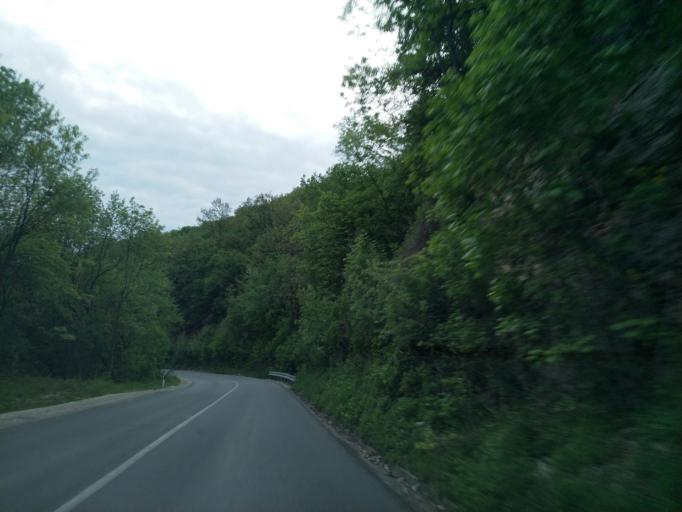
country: RS
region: Central Serbia
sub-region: Pomoravski Okrug
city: Despotovac
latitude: 43.9752
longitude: 21.5109
